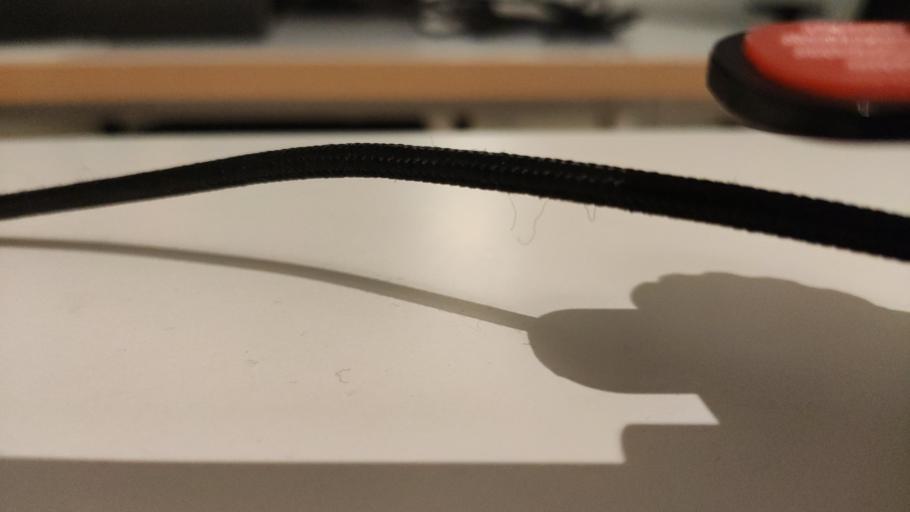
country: RU
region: Moskovskaya
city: Novosin'kovo
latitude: 56.3904
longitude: 37.3106
